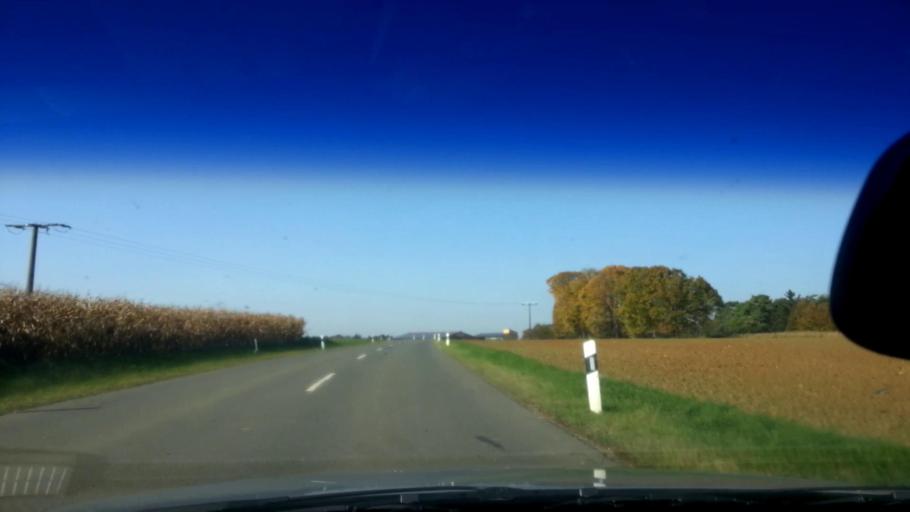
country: DE
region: Bavaria
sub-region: Upper Franconia
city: Wonsees
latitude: 49.9777
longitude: 11.2934
